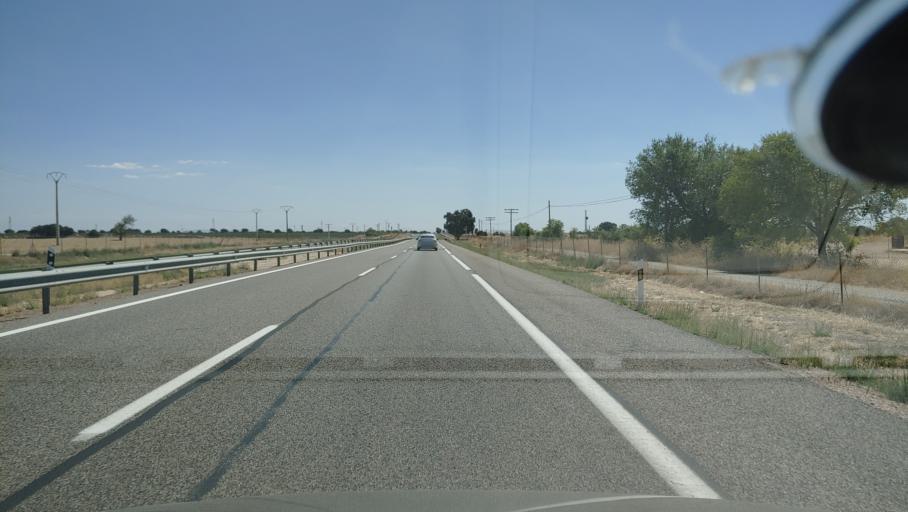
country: ES
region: Castille-La Mancha
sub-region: Provincia de Ciudad Real
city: Villarta de San Juan
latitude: 39.2050
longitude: -3.4078
